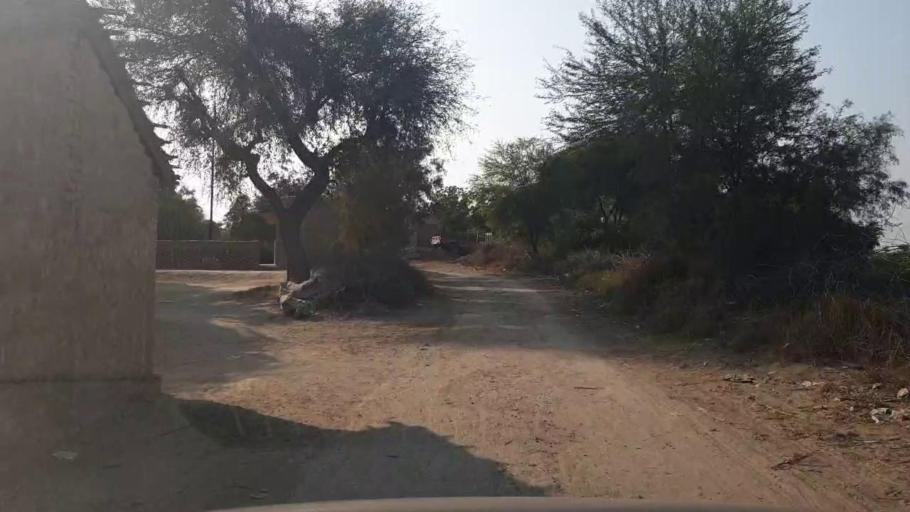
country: PK
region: Sindh
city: Hala
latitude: 25.8555
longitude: 68.3606
